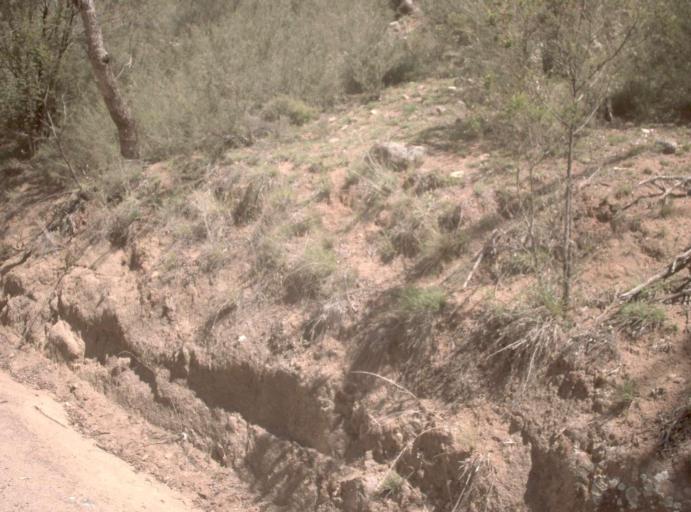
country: AU
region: New South Wales
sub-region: Snowy River
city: Jindabyne
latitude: -37.0351
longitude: 148.5426
